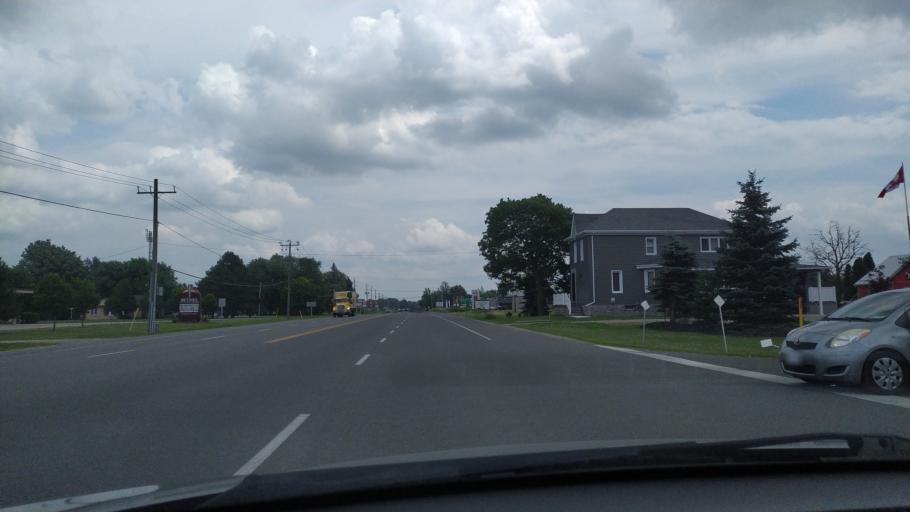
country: CA
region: Ontario
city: Stratford
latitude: 43.3706
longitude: -80.9381
